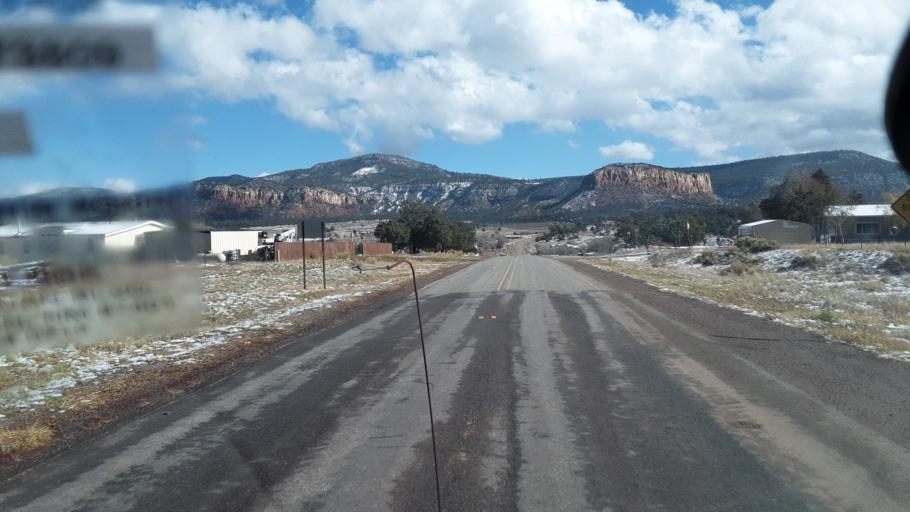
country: US
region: New Mexico
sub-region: Rio Arriba County
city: Santa Teresa
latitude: 36.2291
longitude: -106.8168
